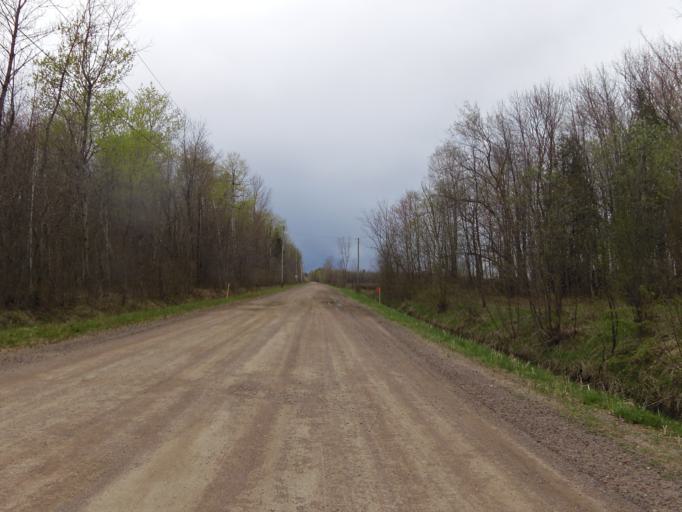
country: CA
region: Ontario
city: Hawkesbury
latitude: 45.6158
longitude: -74.5114
